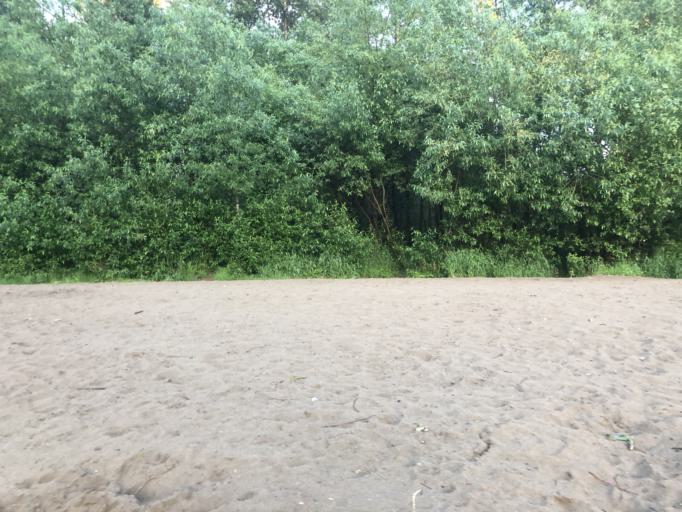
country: US
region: Washington
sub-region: King County
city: Lea Hill
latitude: 47.3040
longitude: -122.1976
